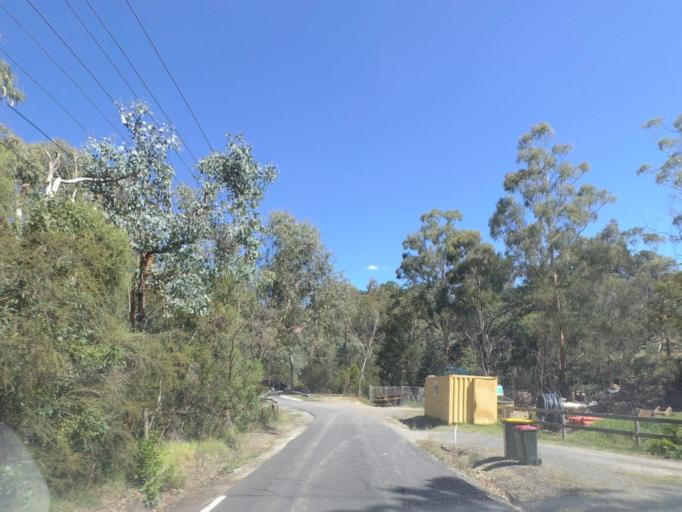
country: AU
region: Victoria
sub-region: Manningham
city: Park Orchards
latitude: -37.7946
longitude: 145.2166
